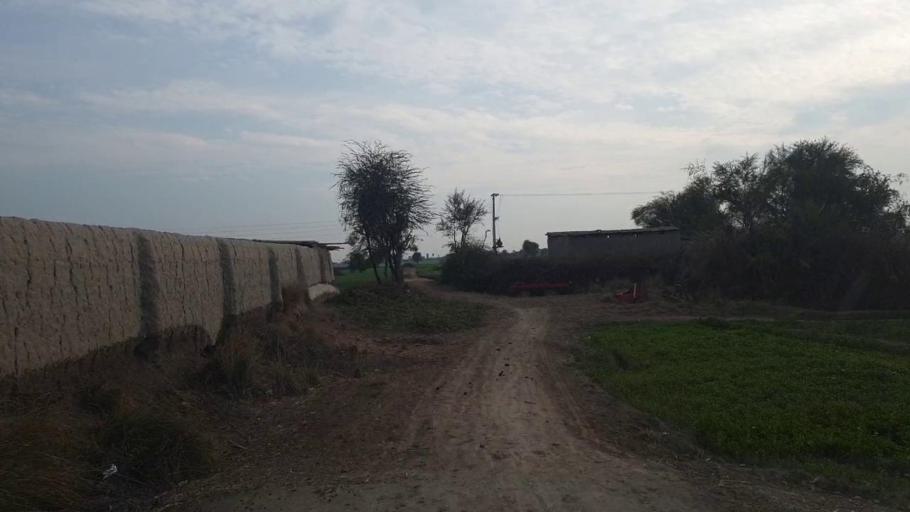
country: PK
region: Sindh
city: Shahpur Chakar
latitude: 26.0619
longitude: 68.5484
